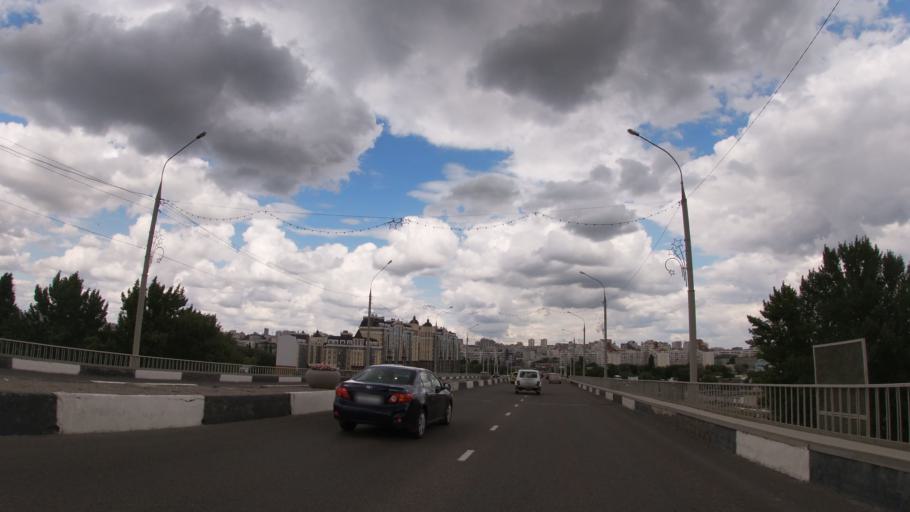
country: RU
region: Belgorod
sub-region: Belgorodskiy Rayon
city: Belgorod
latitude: 50.5859
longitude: 36.5870
